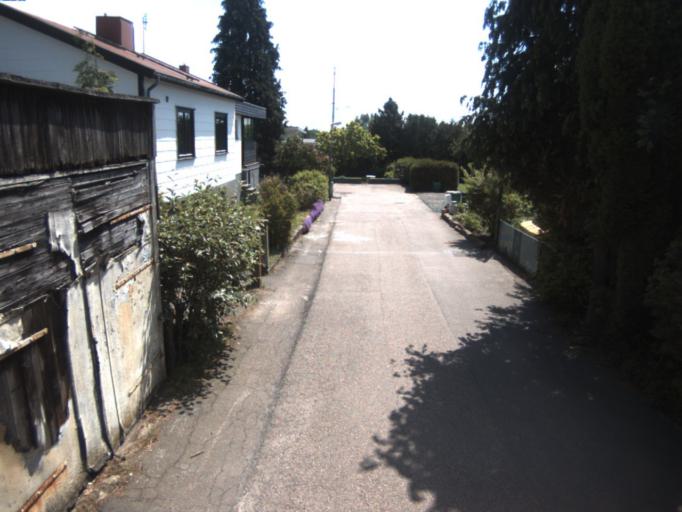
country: SE
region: Skane
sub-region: Helsingborg
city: Barslov
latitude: 56.0269
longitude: 12.8077
